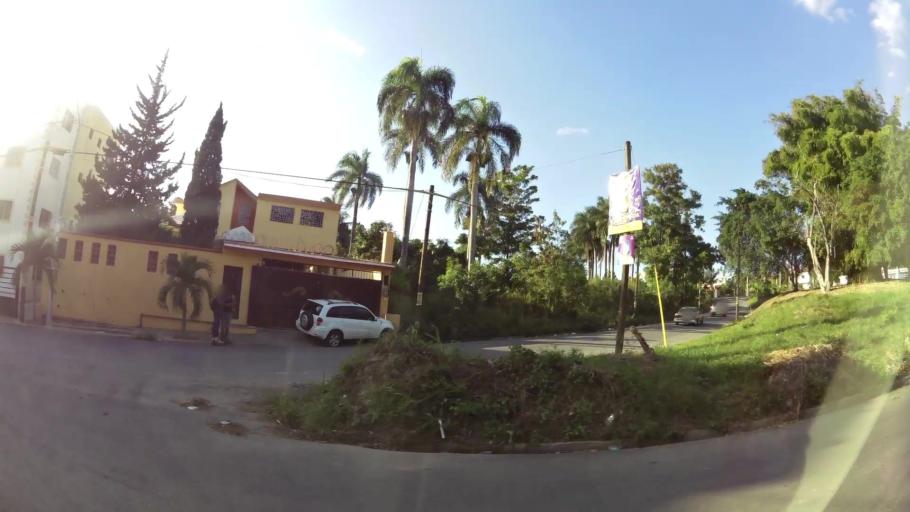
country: DO
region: Nacional
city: Ensanche Luperon
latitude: 18.5489
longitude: -69.9039
